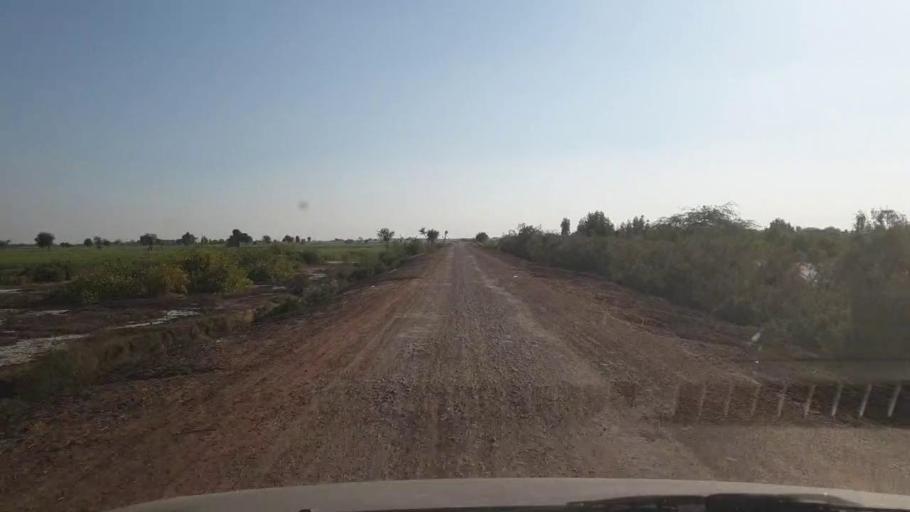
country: PK
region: Sindh
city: Mirwah Gorchani
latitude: 25.3672
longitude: 69.0969
